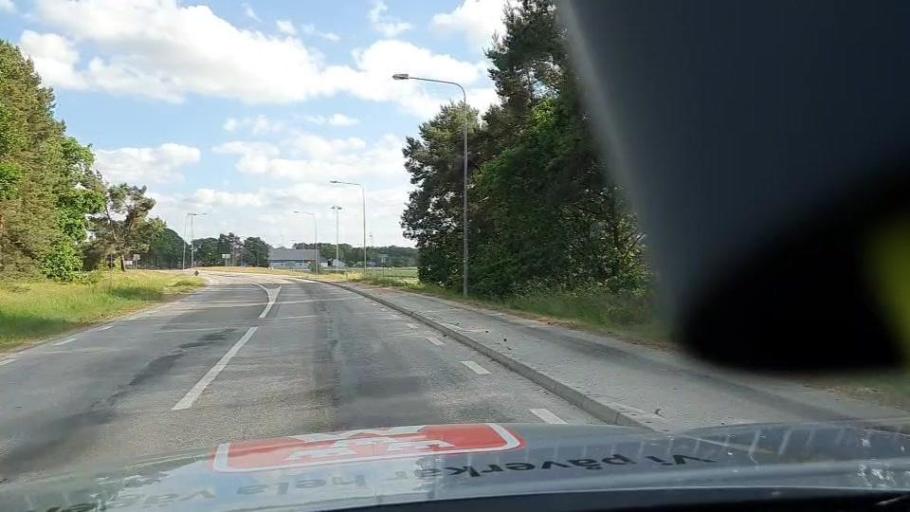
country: SE
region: Blekinge
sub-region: Karlshamns Kommun
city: Morrum
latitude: 56.1133
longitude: 14.6752
